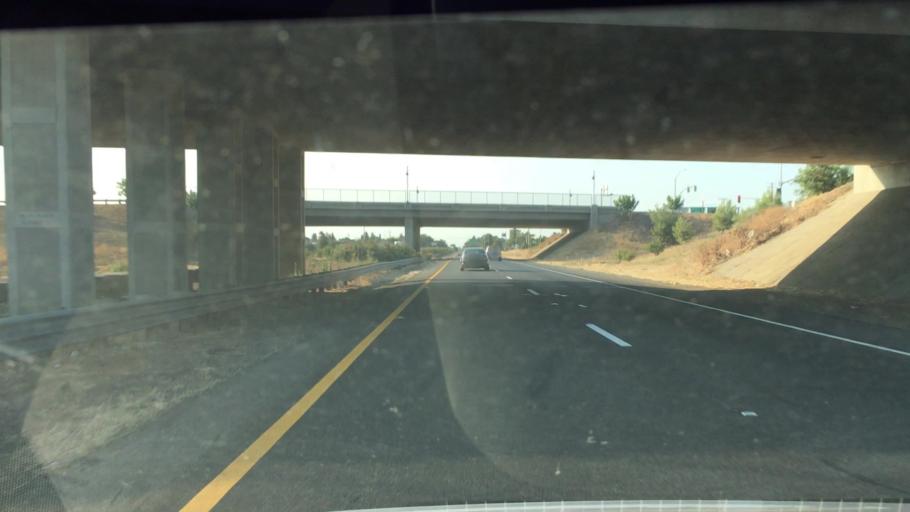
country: US
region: California
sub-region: Sacramento County
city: Galt
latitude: 38.2555
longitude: -121.2944
